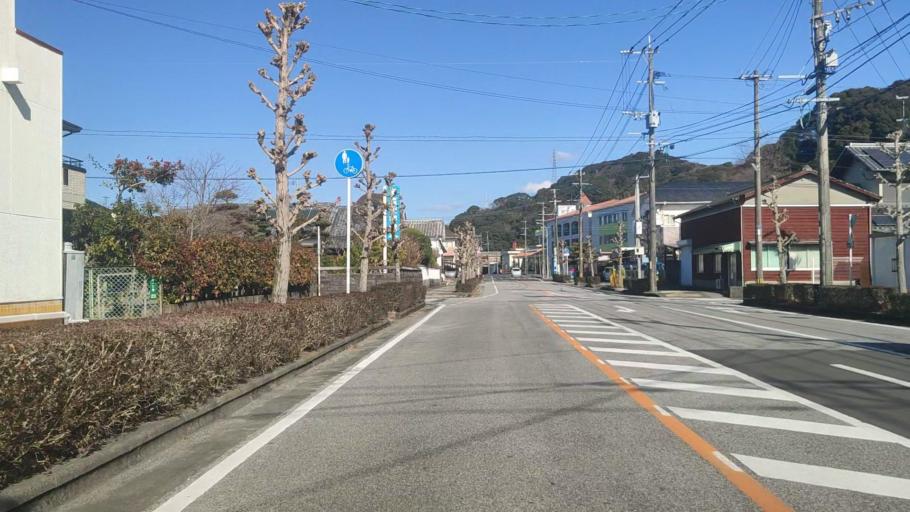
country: JP
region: Oita
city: Saiki
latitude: 32.9624
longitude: 131.9080
